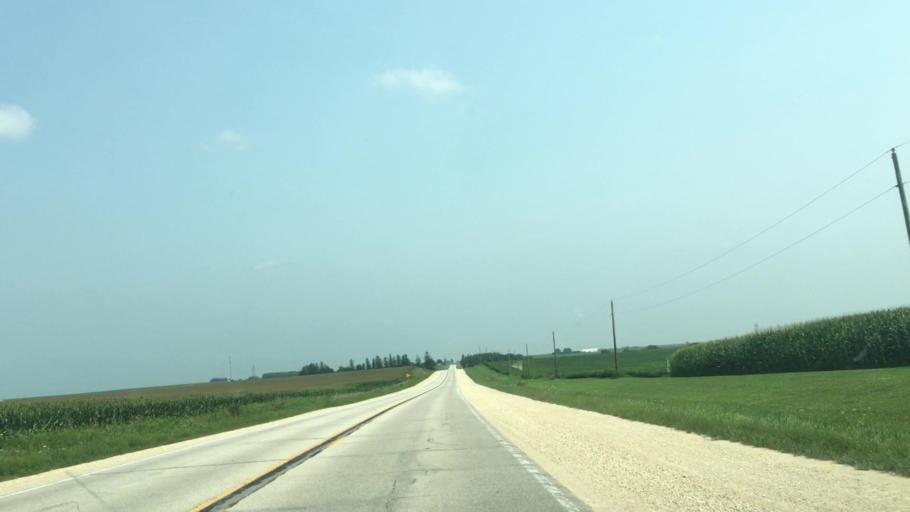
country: US
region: Iowa
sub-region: Fayette County
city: Oelwein
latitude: 42.6798
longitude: -91.8626
